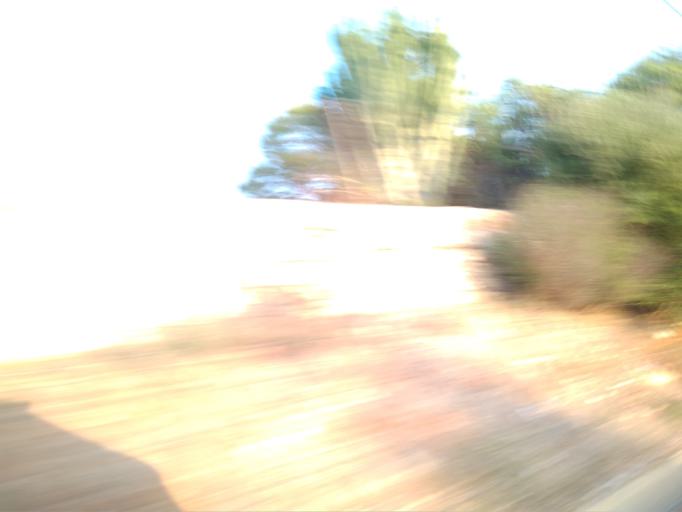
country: PT
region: Faro
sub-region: Faro
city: Santa Barbara de Nexe
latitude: 37.0951
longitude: -7.9631
